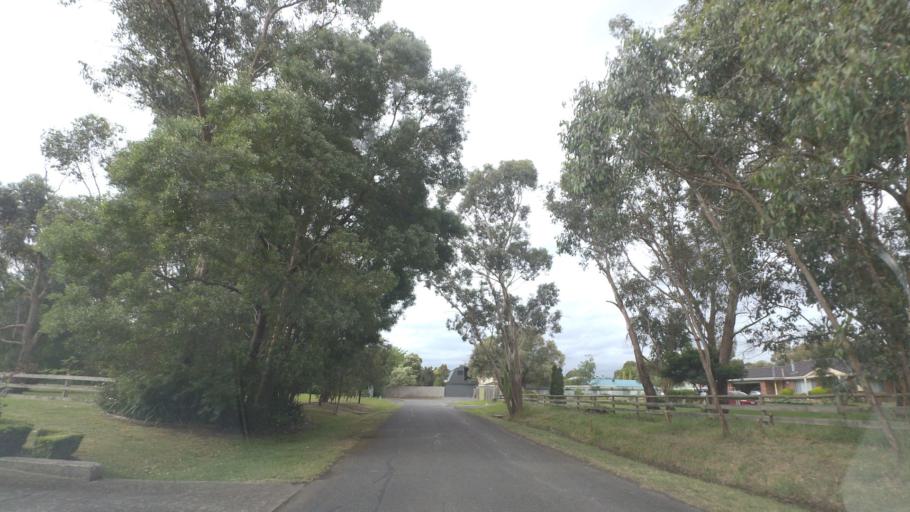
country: AU
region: Victoria
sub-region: Maroondah
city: Kilsyth South
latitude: -37.8238
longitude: 145.3103
